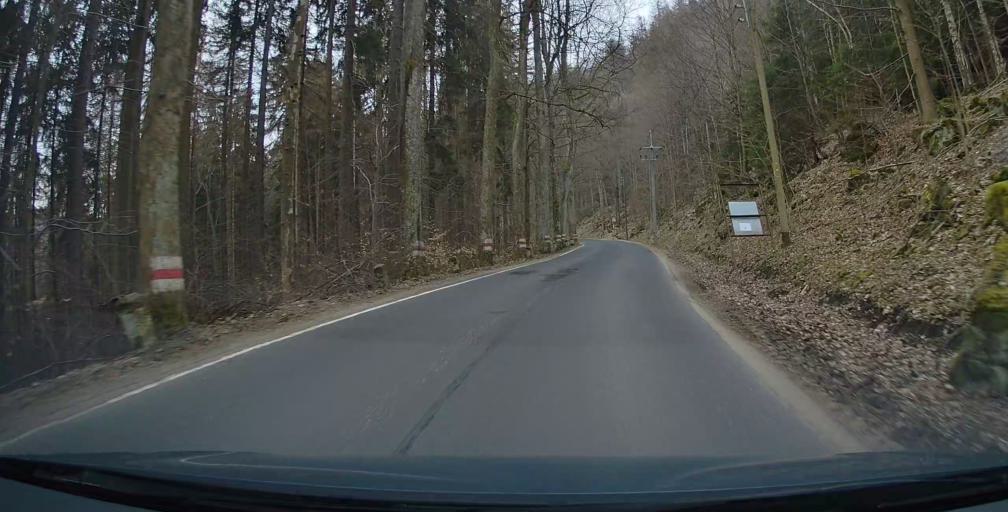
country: PL
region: Lower Silesian Voivodeship
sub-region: Powiat klodzki
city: Radkow
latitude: 50.4848
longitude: 16.3830
